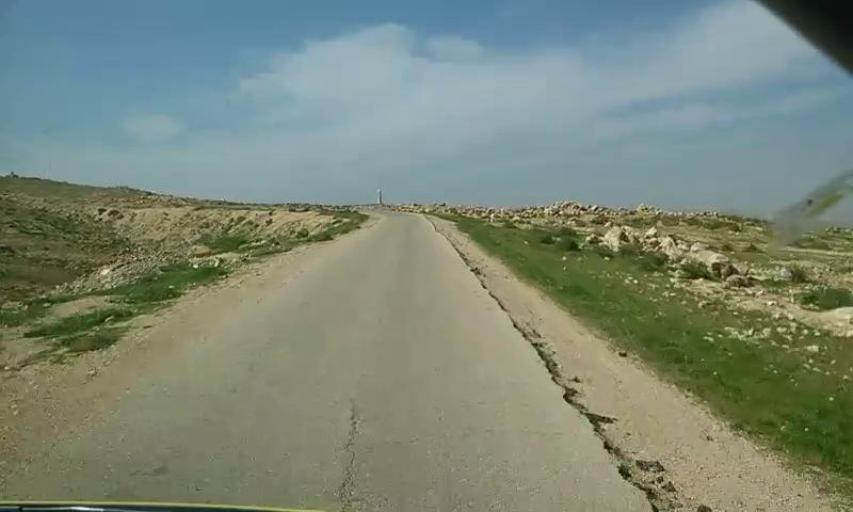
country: PS
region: West Bank
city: Khallat al Mayyah
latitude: 31.4408
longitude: 35.2047
